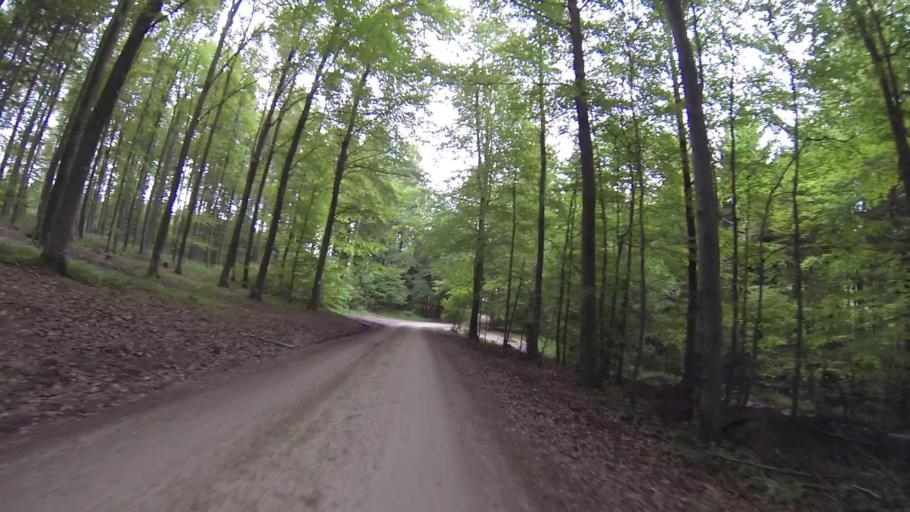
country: DE
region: Baden-Wuerttemberg
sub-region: Regierungsbezirk Stuttgart
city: Heubach
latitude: 48.7449
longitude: 9.8880
